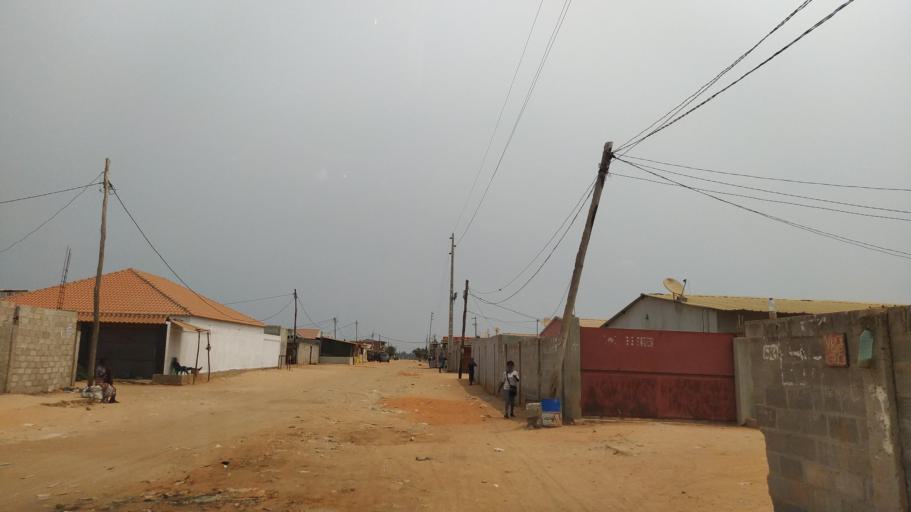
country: AO
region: Luanda
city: Luanda
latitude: -9.0736
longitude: 13.4023
